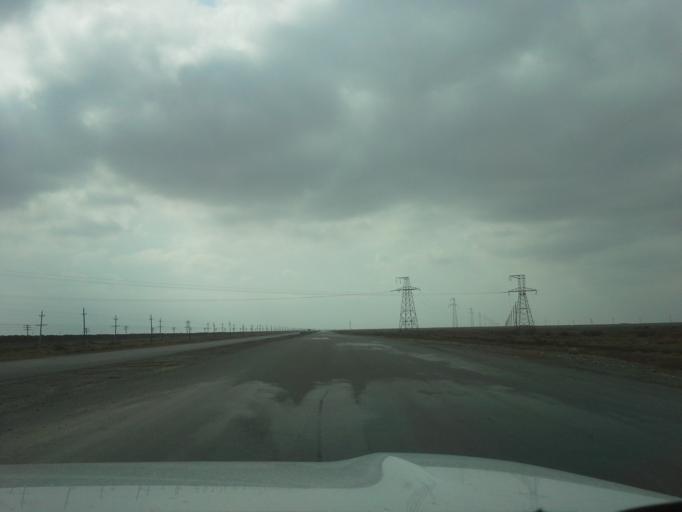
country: IR
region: Razavi Khorasan
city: Kalat-e Naderi
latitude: 37.2153
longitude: 60.0933
